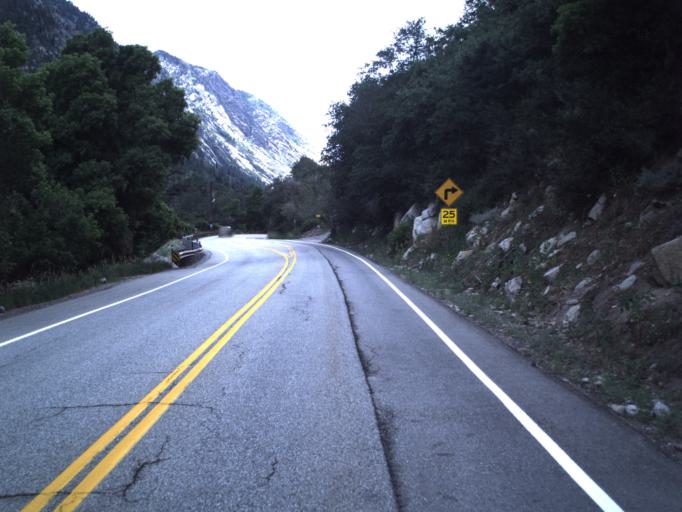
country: US
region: Utah
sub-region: Salt Lake County
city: Granite
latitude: 40.5718
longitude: -111.7365
